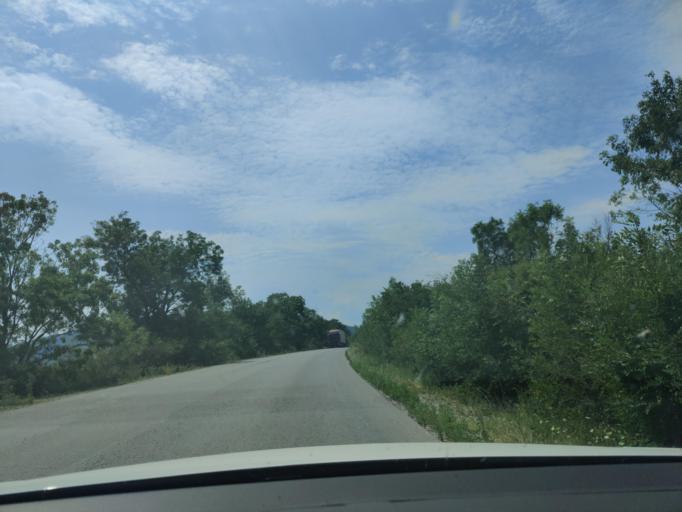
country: BG
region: Montana
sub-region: Obshtina Montana
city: Montana
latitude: 43.4771
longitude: 23.0908
